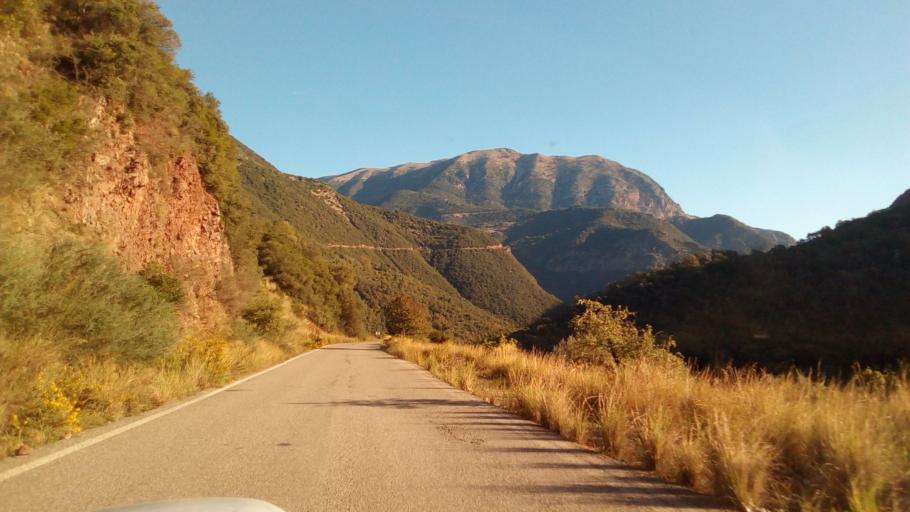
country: GR
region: West Greece
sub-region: Nomos Aitolias kai Akarnanias
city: Nafpaktos
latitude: 38.4584
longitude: 21.8805
